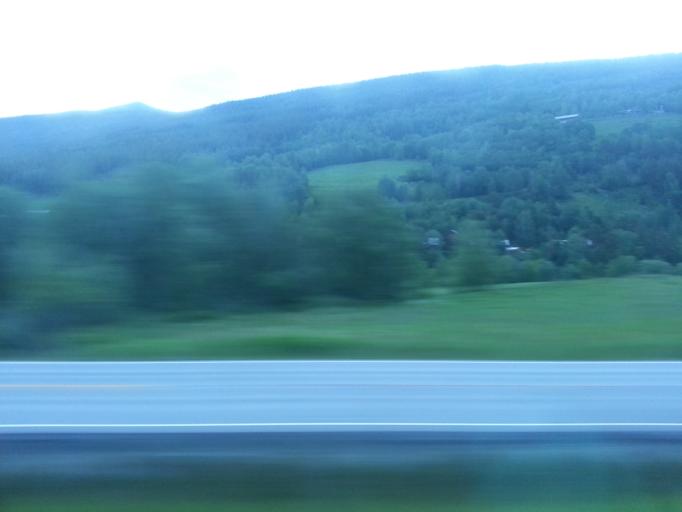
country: NO
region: Oppland
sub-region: Dovre
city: Dovre
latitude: 61.8991
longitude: 9.3798
